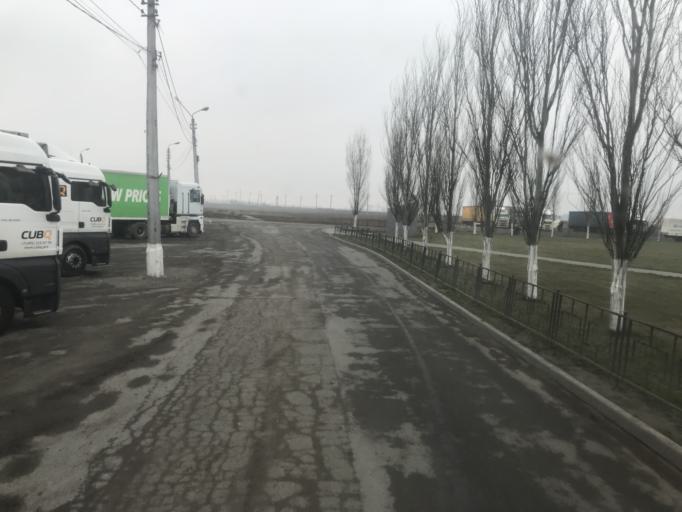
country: RU
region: Volgograd
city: Svetlyy Yar
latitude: 48.4905
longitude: 44.6621
